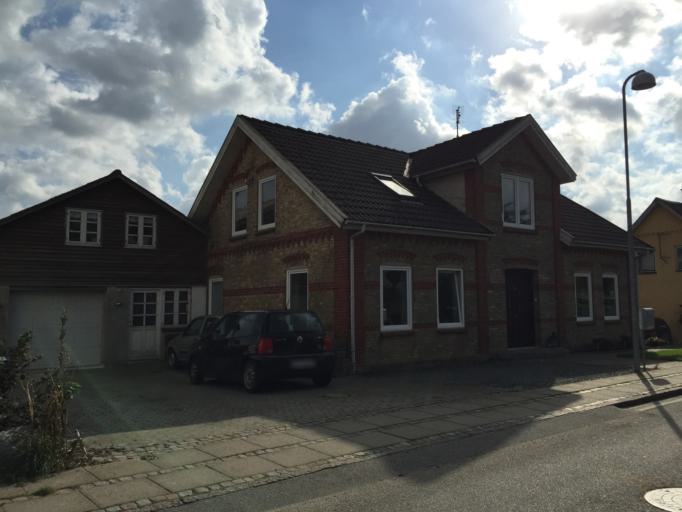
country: DK
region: South Denmark
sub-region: Sonderborg Kommune
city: Grasten
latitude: 54.9973
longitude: 9.5821
